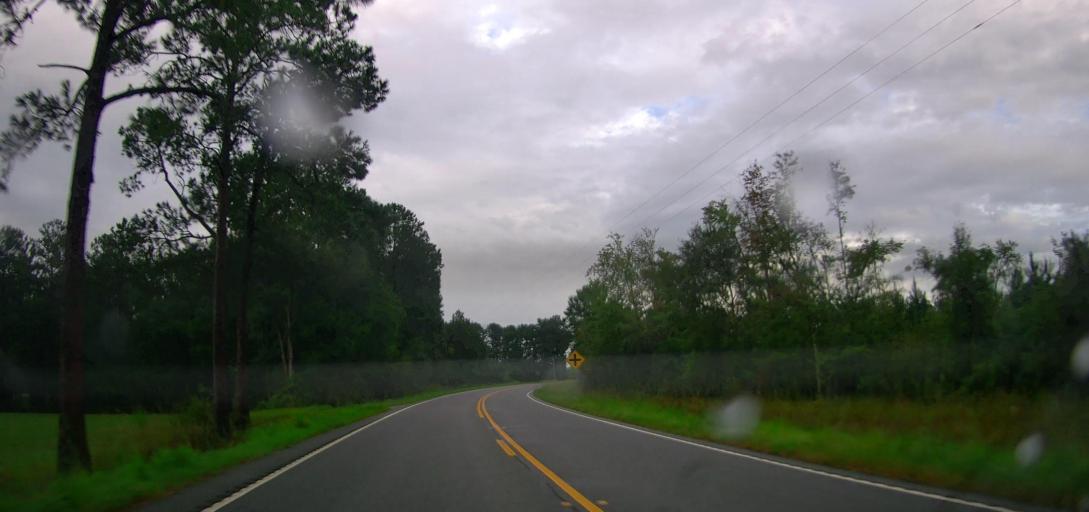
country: US
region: Georgia
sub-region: Ware County
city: Deenwood
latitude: 31.2776
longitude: -82.4198
